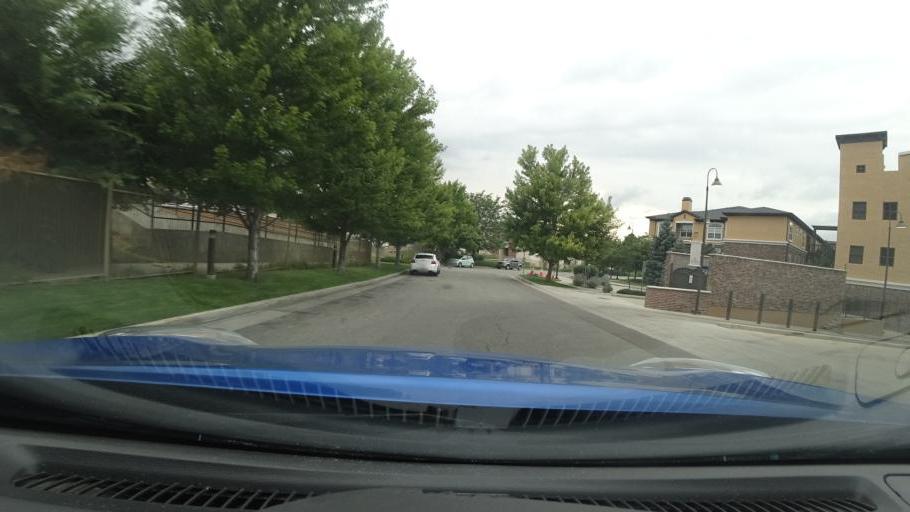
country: US
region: Colorado
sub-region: Adams County
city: Aurora
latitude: 39.6996
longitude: -104.8203
